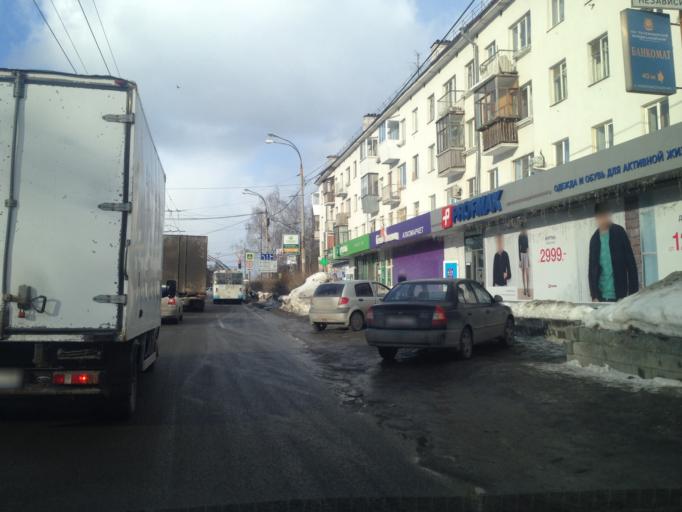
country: RU
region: Sverdlovsk
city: Yekaterinburg
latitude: 56.8565
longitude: 60.6541
